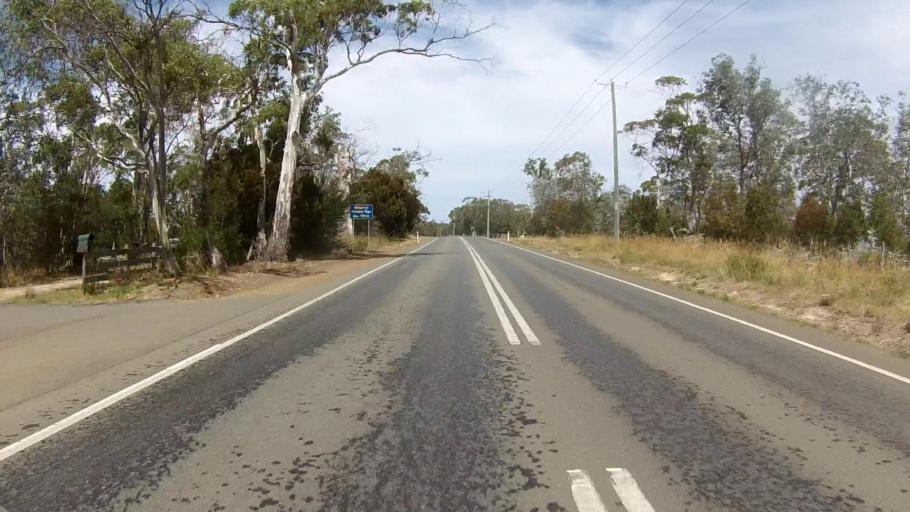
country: AU
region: Tasmania
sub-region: Clarence
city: Sandford
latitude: -42.9710
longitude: 147.5034
